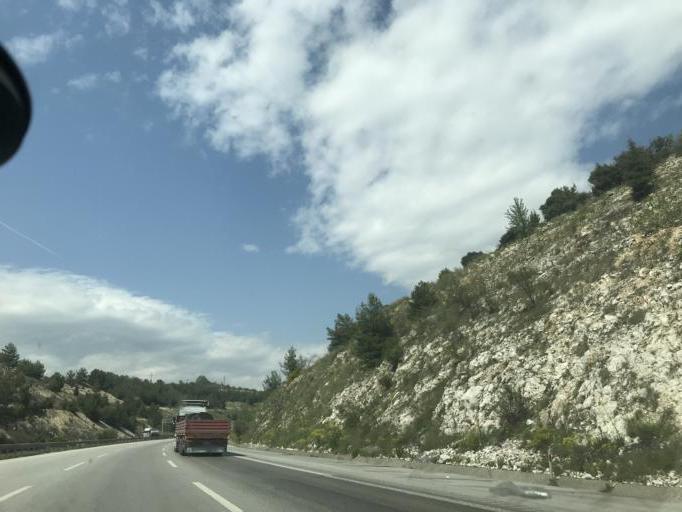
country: TR
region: Mersin
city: Tarsus
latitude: 37.1538
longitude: 34.8394
